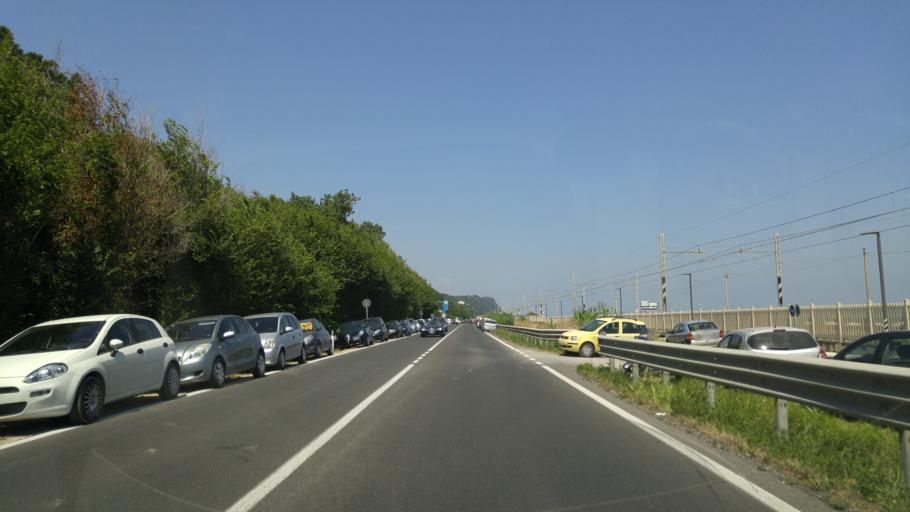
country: IT
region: The Marches
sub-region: Provincia di Pesaro e Urbino
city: Fenile
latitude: 43.8740
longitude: 12.9723
